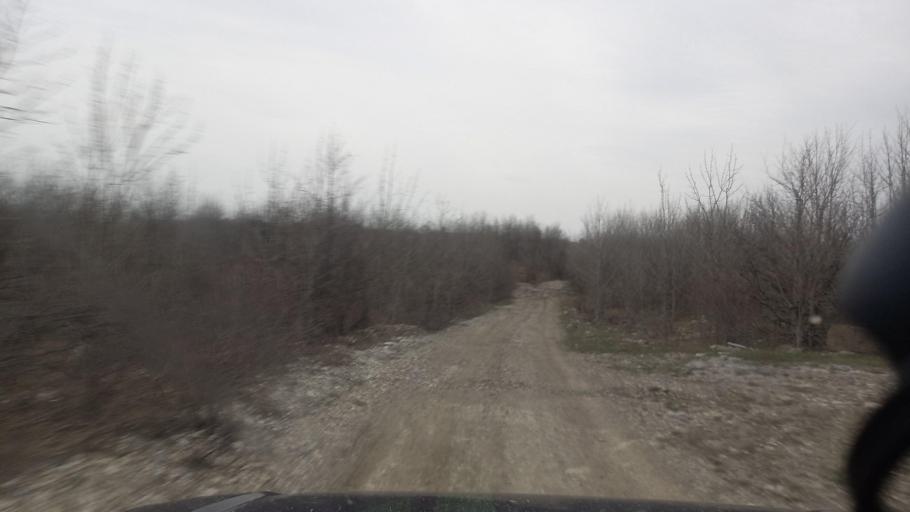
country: RU
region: Krasnodarskiy
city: Pshada
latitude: 44.5975
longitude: 38.2881
